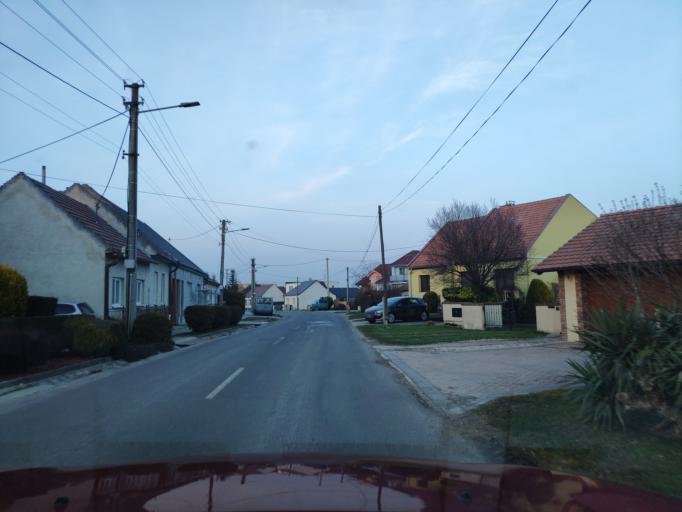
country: SK
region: Trnavsky
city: Leopoldov
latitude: 48.4596
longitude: 17.7164
